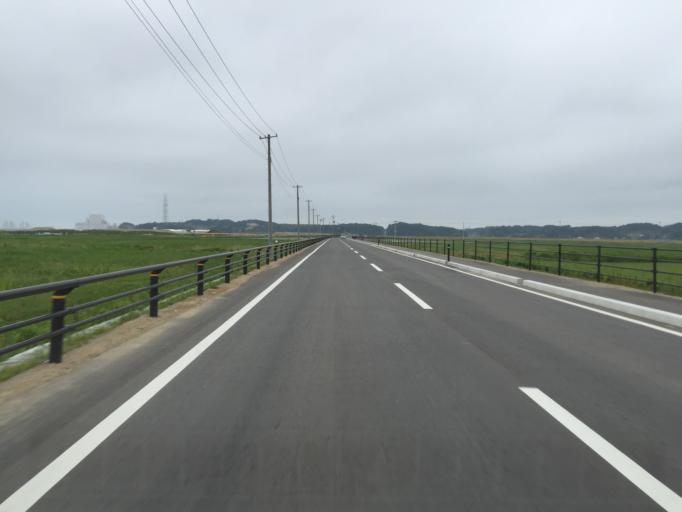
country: JP
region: Fukushima
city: Namie
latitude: 37.6945
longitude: 141.0057
